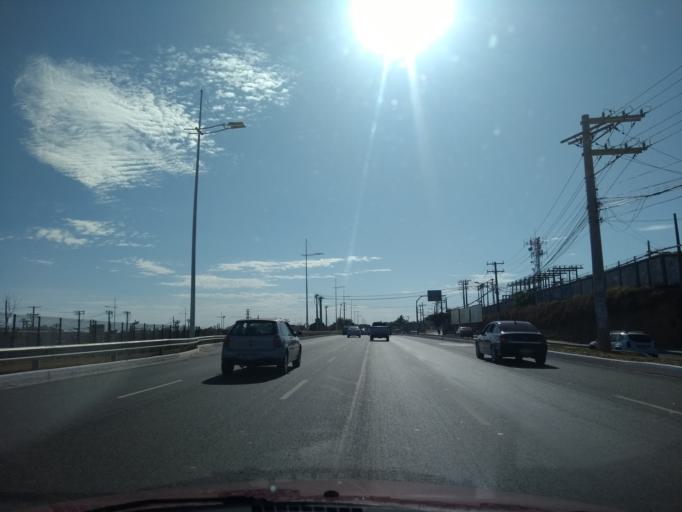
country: BR
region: Bahia
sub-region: Lauro De Freitas
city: Lauro de Freitas
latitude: -12.9212
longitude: -38.3591
